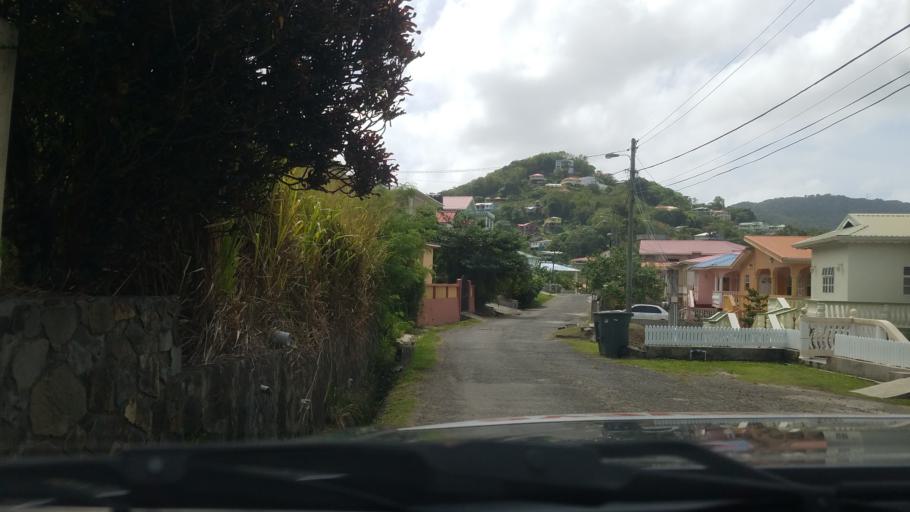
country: LC
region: Gros-Islet
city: Gros Islet
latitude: 14.0456
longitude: -60.9588
